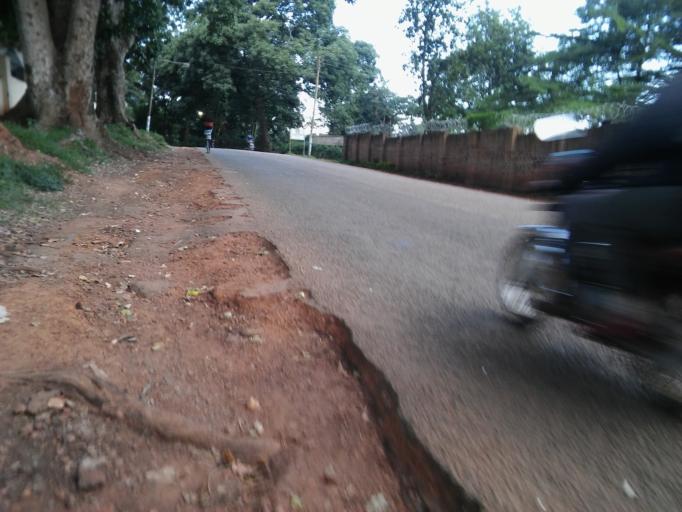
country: UG
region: Eastern Region
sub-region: Mbale District
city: Mbale
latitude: 1.0646
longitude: 34.1982
